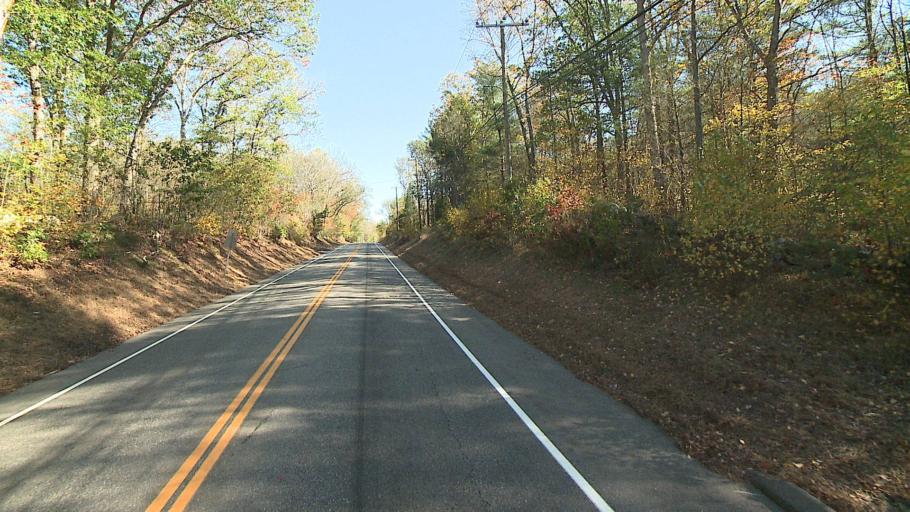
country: US
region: Connecticut
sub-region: Tolland County
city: Storrs
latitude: 41.8652
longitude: -72.1571
